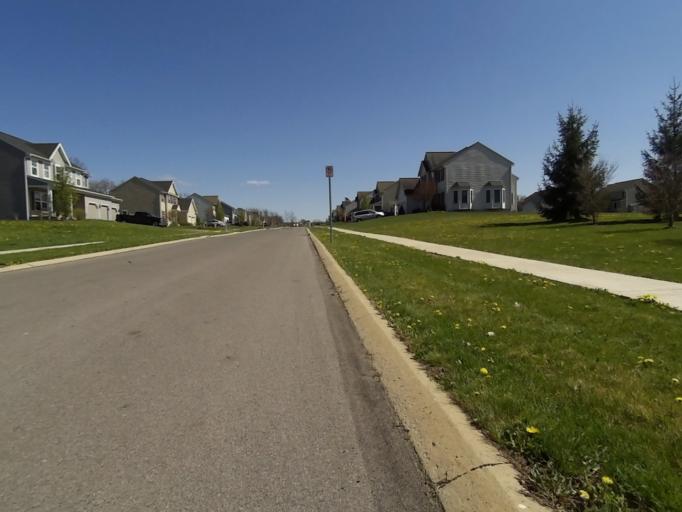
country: US
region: Pennsylvania
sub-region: Centre County
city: Houserville
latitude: 40.8833
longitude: -77.8336
